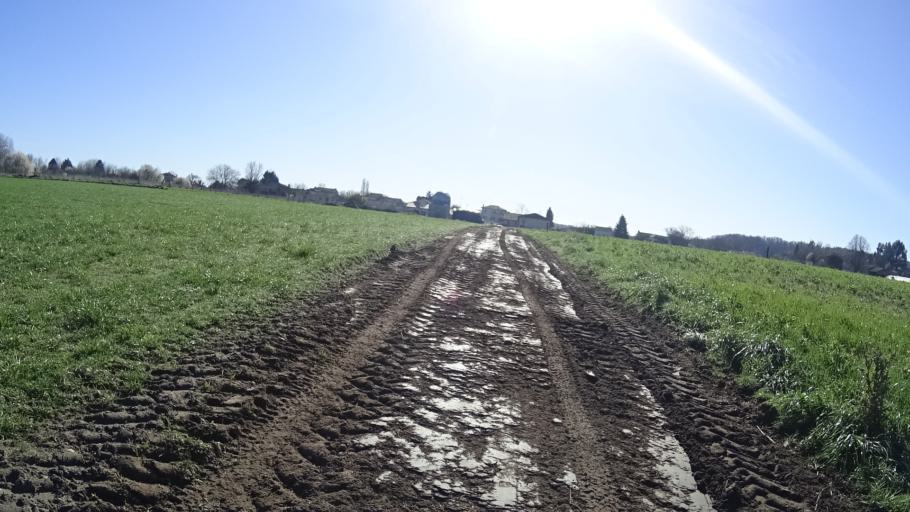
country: FR
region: Aquitaine
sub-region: Departement de la Dordogne
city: Saint-Aulaye
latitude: 45.2198
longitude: 0.0975
